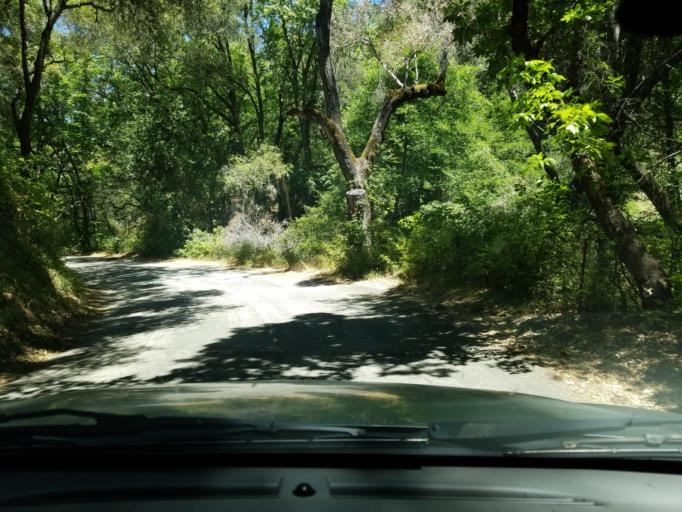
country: US
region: California
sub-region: Monterey County
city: Gonzales
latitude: 36.3656
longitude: -121.5564
